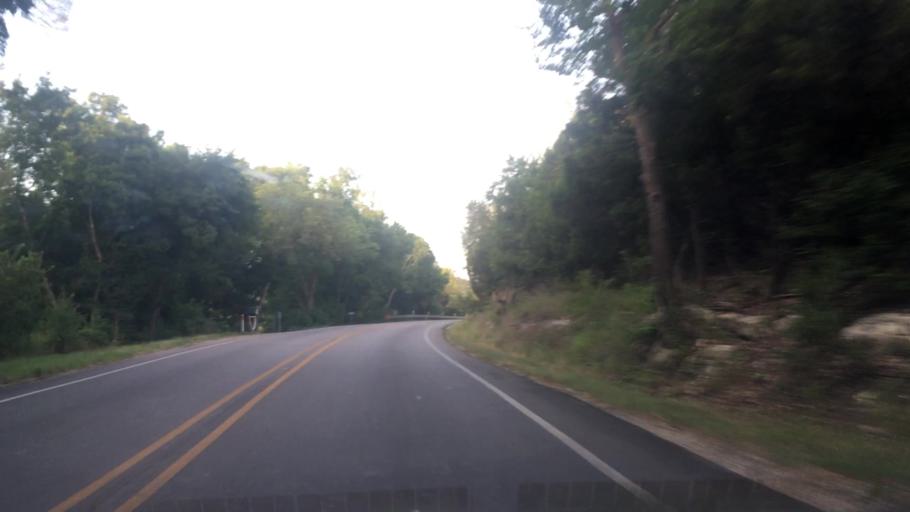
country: US
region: Texas
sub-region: Williamson County
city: Anderson Mill
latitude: 30.4452
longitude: -97.8621
